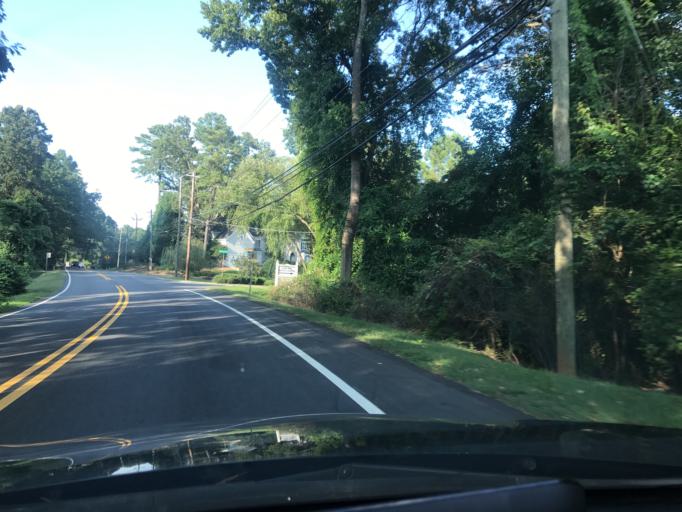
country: US
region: Georgia
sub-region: DeKalb County
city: North Druid Hills
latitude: 33.8259
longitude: -84.2832
